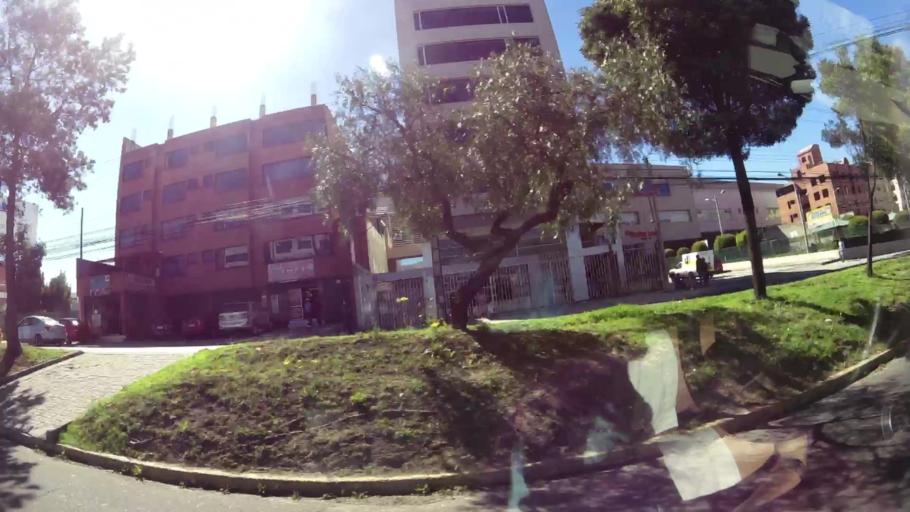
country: EC
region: Pichincha
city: Quito
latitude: -0.1385
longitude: -78.4700
